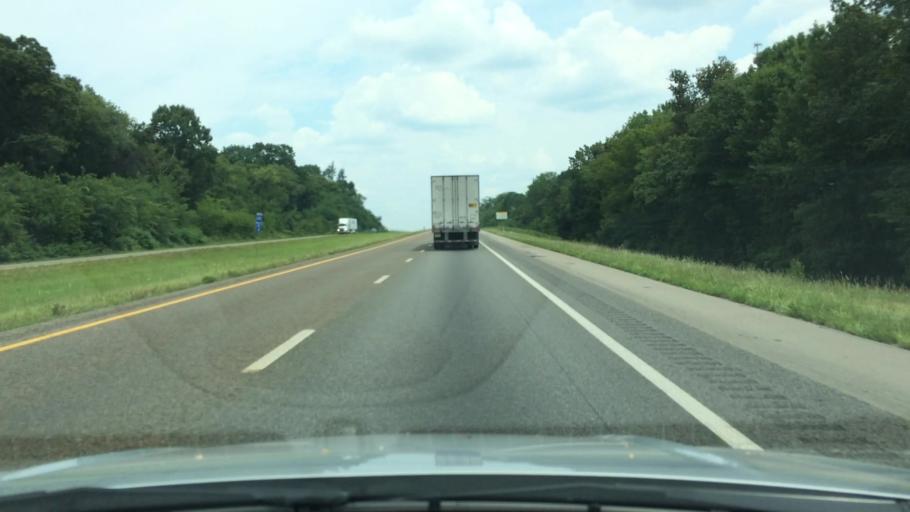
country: US
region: Tennessee
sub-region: Maury County
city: Spring Hill
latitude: 35.6319
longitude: -86.8958
